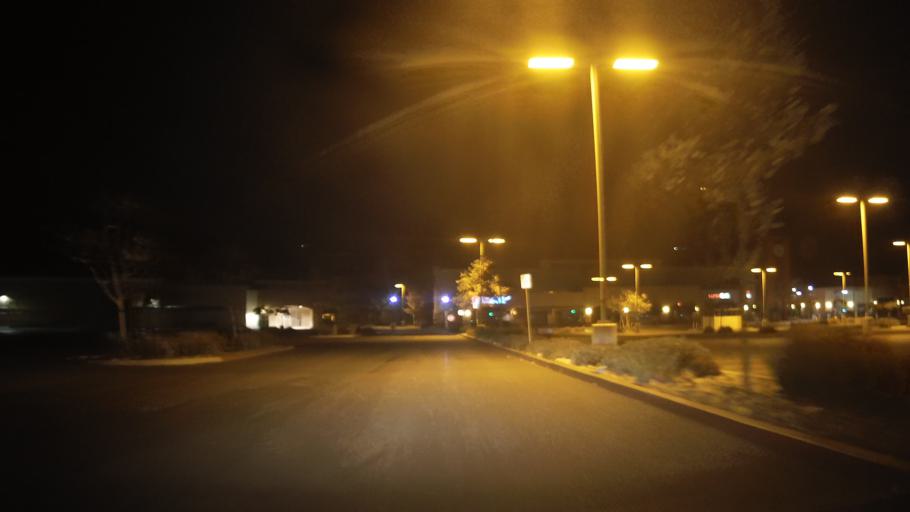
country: US
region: California
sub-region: San Diego County
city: Rancho San Diego
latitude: 32.7391
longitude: -116.9401
